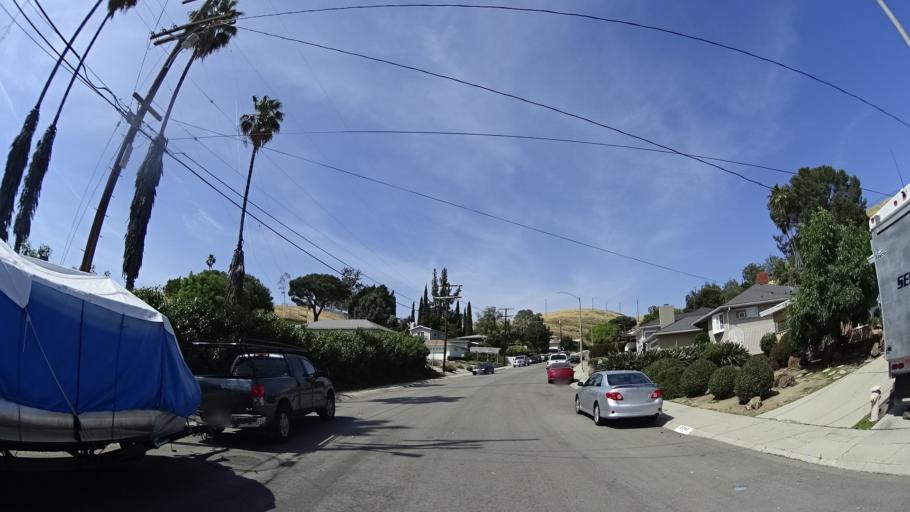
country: US
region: California
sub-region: Los Angeles County
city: Belvedere
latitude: 34.0703
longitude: -118.1929
